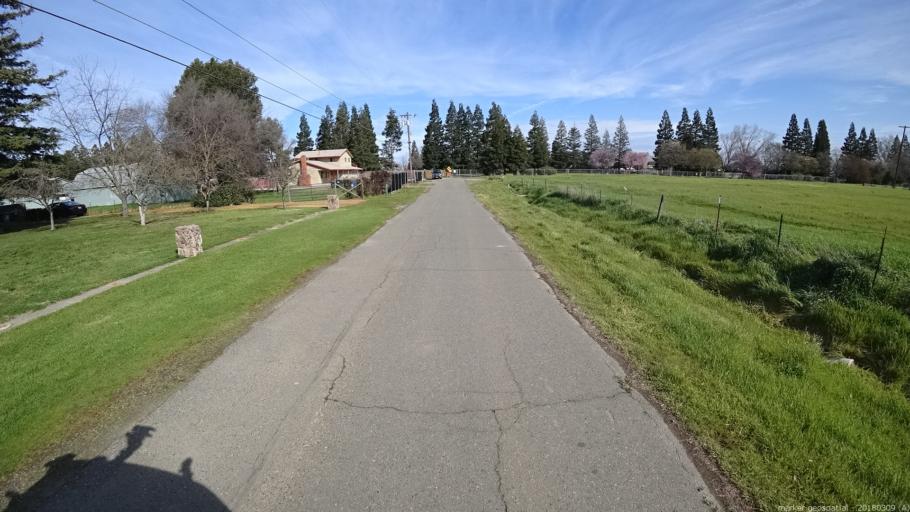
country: US
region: California
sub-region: Sacramento County
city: Florin
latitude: 38.4591
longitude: -121.3902
